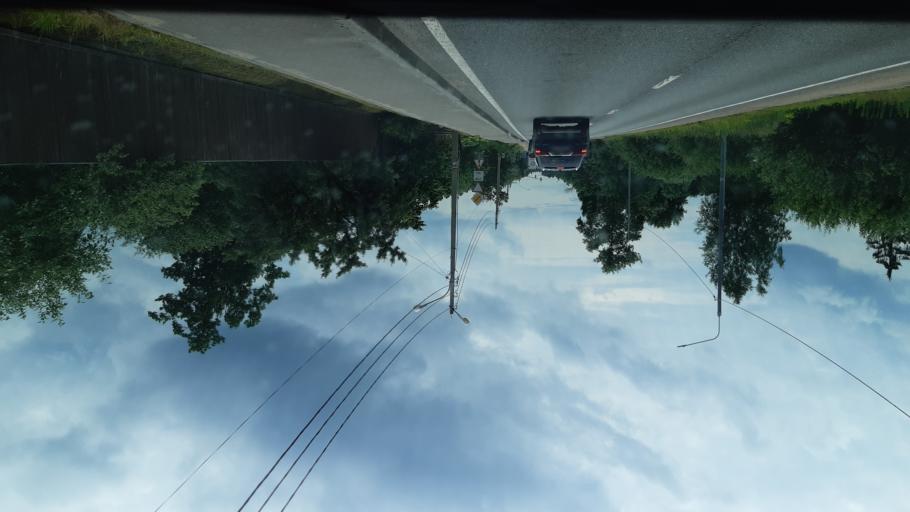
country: RU
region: Moskovskaya
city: Dorokhovo
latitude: 55.5331
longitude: 36.3608
